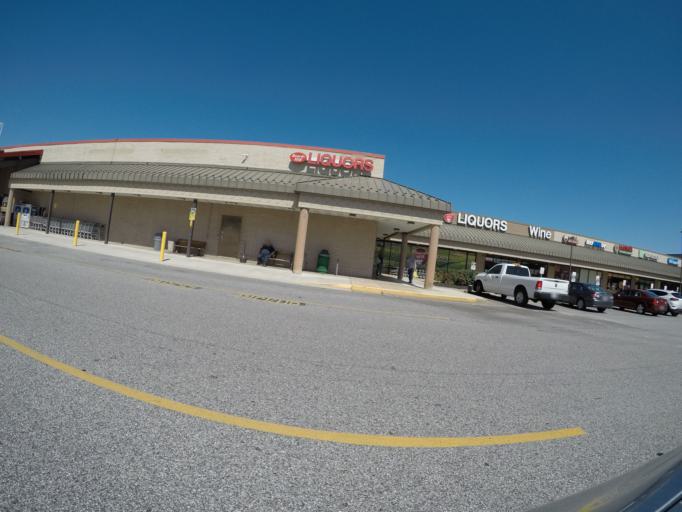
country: US
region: Maryland
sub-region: Harford County
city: Aberdeen
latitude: 39.5248
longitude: -76.1810
